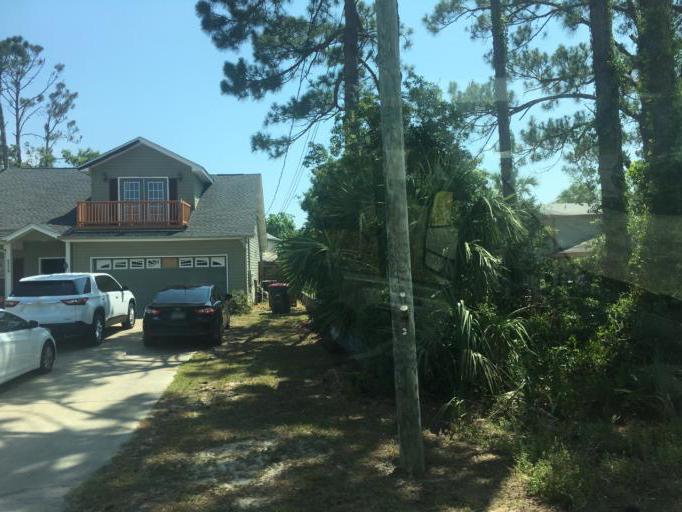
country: US
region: Florida
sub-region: Bay County
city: Lower Grand Lagoon
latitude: 30.1574
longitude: -85.7680
